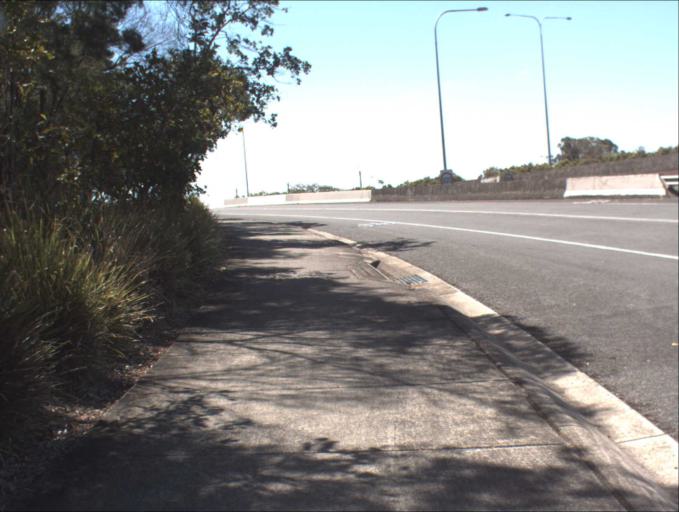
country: AU
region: Queensland
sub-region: Logan
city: Beenleigh
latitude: -27.7055
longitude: 153.2021
